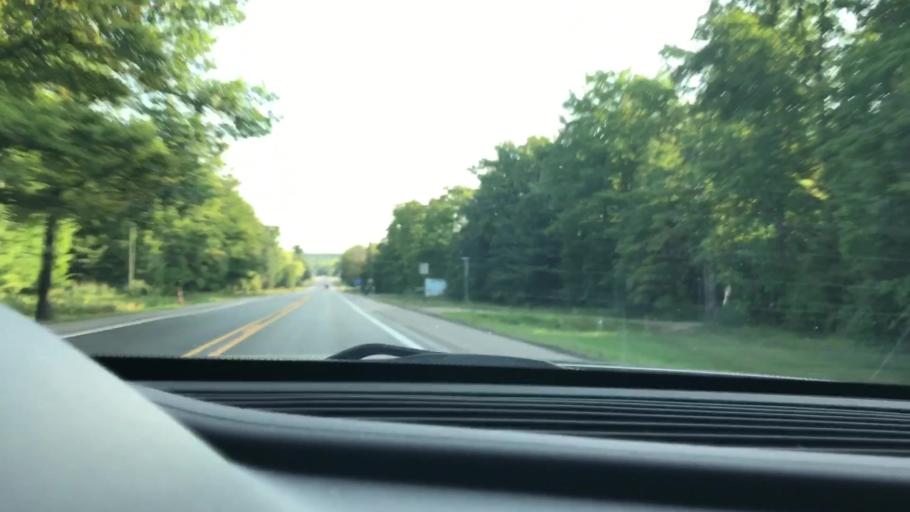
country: US
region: Michigan
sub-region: Antrim County
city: Bellaire
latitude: 45.1008
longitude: -85.3578
